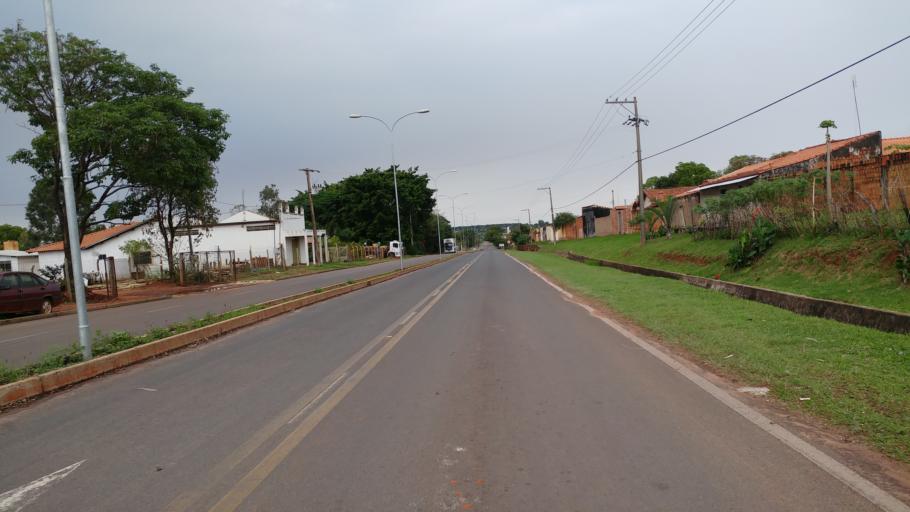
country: BR
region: Sao Paulo
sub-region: Paraguacu Paulista
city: Paraguacu Paulista
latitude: -22.4336
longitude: -50.5797
